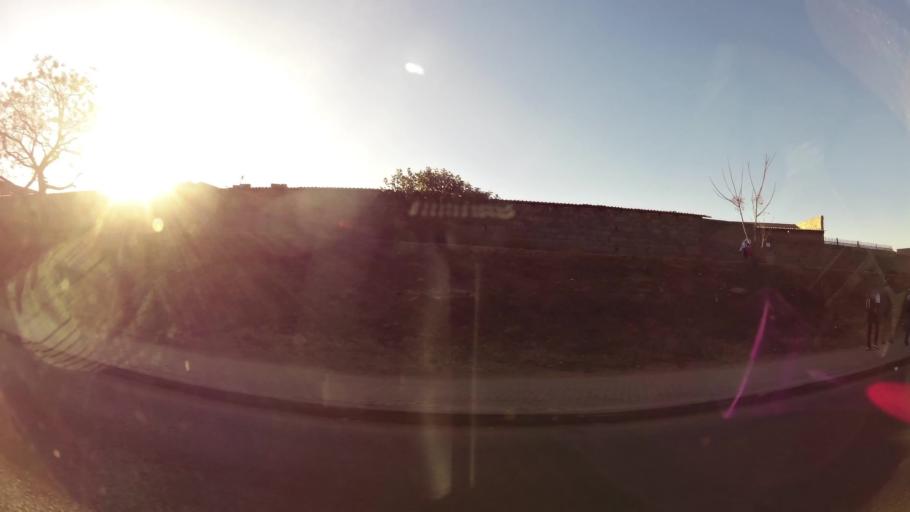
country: ZA
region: Gauteng
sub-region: Ekurhuleni Metropolitan Municipality
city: Tembisa
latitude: -26.0153
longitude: 28.2391
